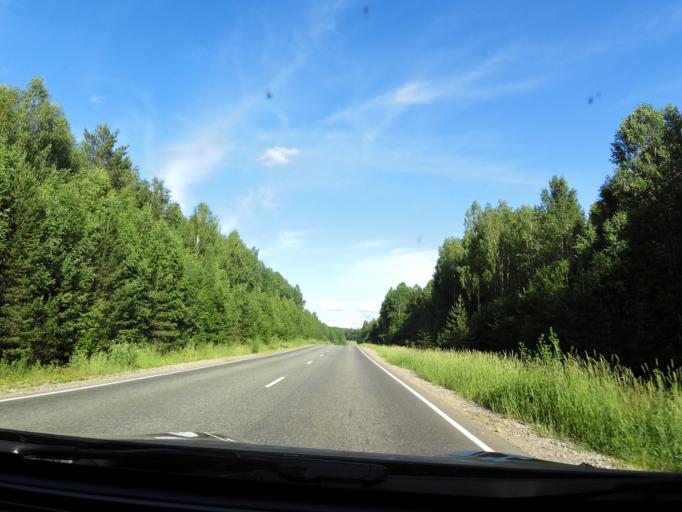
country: RU
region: Kirov
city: Chernaya Kholunitsa
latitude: 58.8608
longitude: 51.6124
